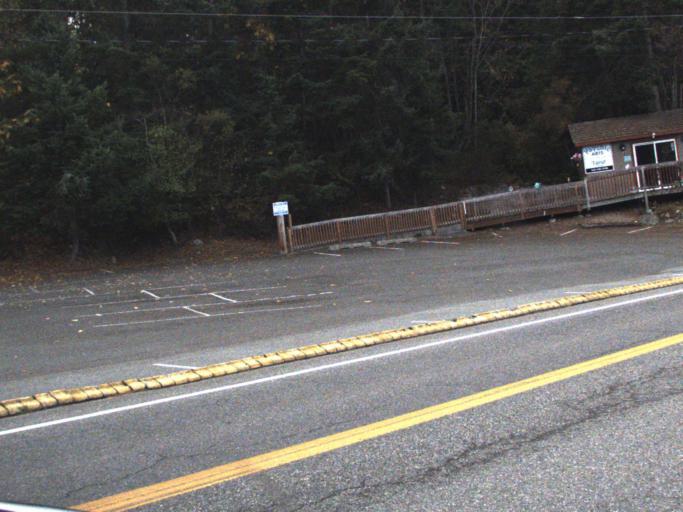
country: US
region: Washington
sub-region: Jefferson County
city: Port Hadlock-Irondale
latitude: 48.0657
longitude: -122.8198
